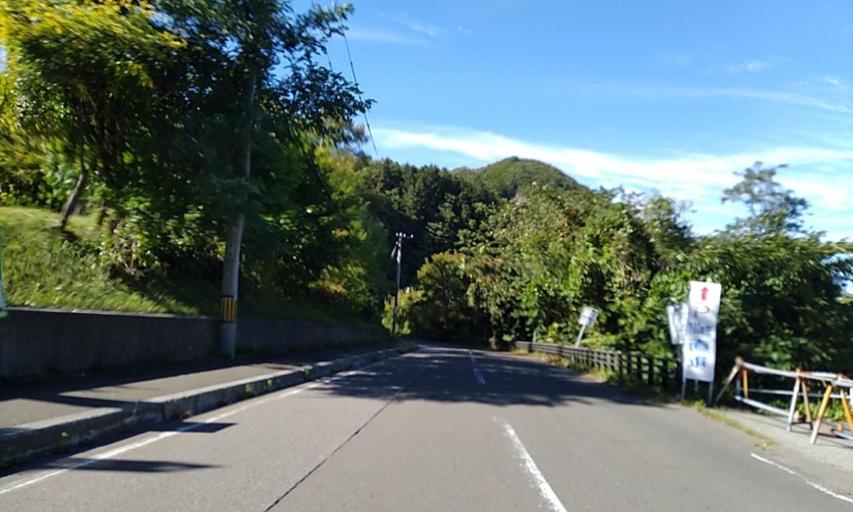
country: JP
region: Hokkaido
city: Sapporo
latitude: 43.0517
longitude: 141.2919
